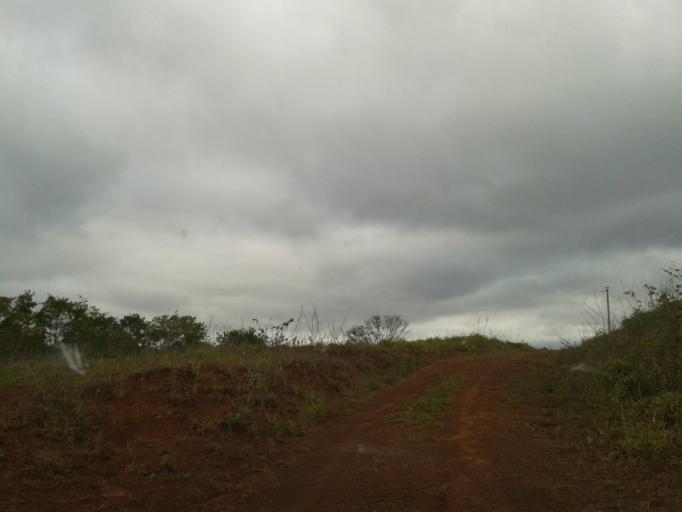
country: BR
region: Minas Gerais
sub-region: Campina Verde
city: Campina Verde
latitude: -19.4851
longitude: -49.6197
